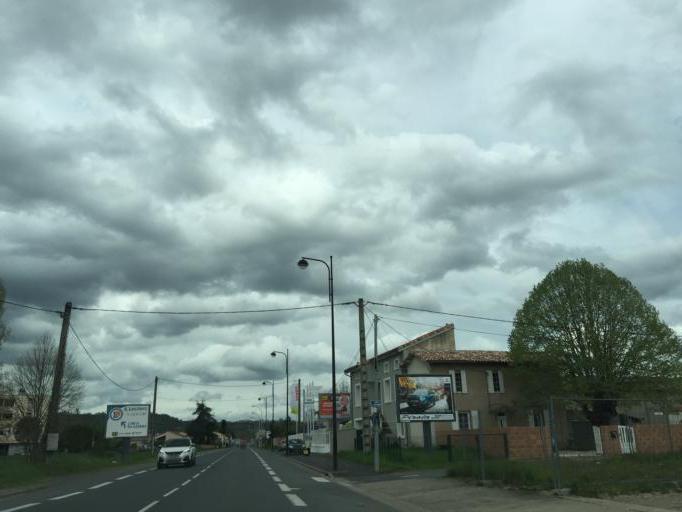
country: FR
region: Midi-Pyrenees
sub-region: Departement du Tarn
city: Albi
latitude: 43.9465
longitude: 2.1518
